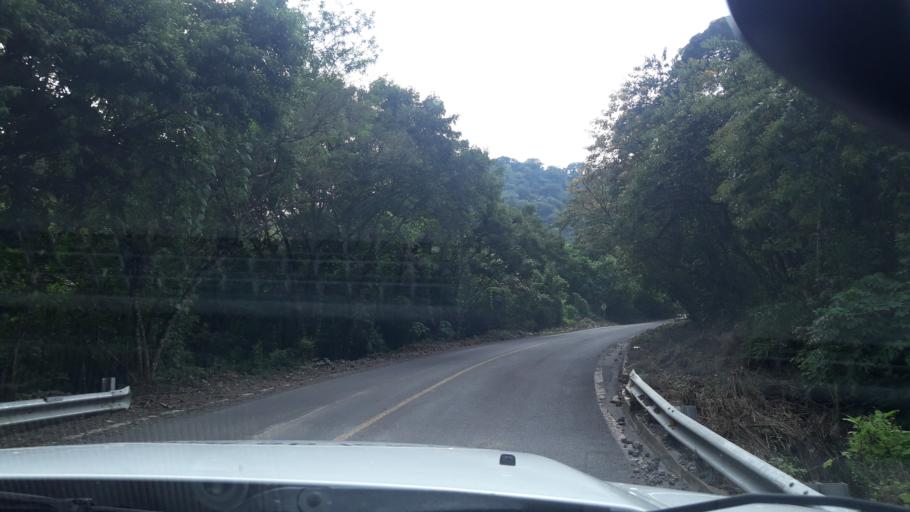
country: MX
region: Colima
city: Suchitlan
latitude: 19.4436
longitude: -103.7145
